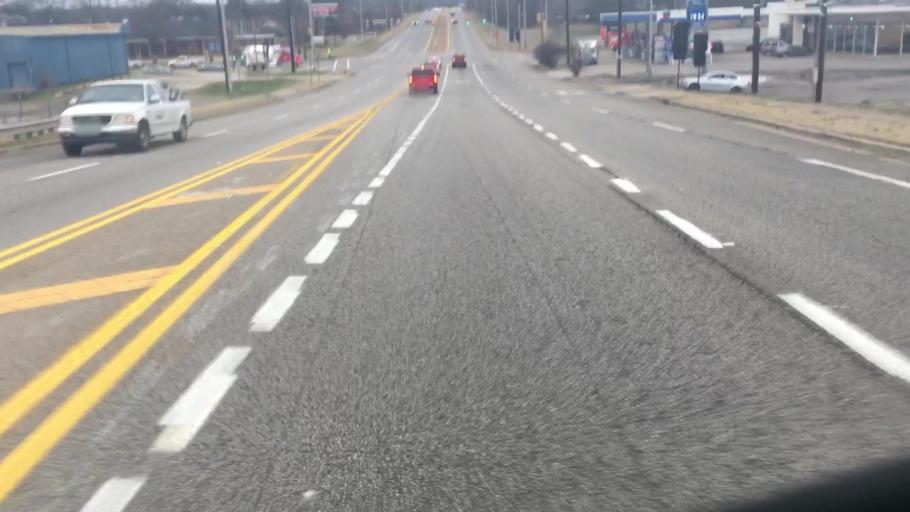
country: US
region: Alabama
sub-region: Jefferson County
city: Birmingham
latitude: 33.5448
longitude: -86.8150
